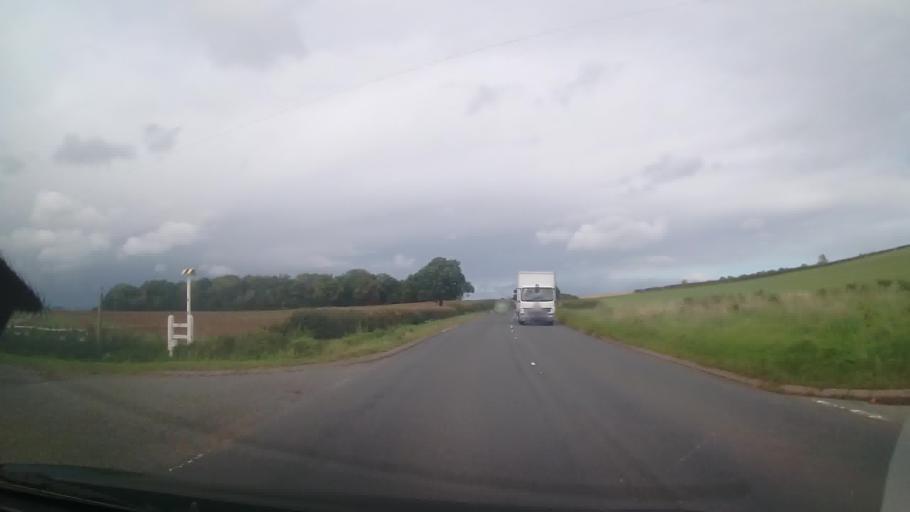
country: GB
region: England
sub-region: Shropshire
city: Alveley
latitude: 52.4748
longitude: -2.3531
